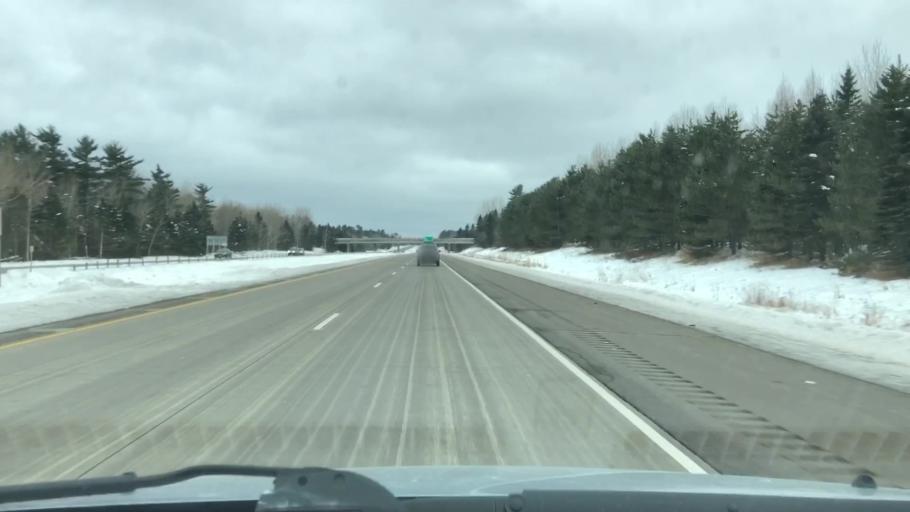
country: US
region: Minnesota
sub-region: Carlton County
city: Esko
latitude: 46.7010
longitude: -92.3167
